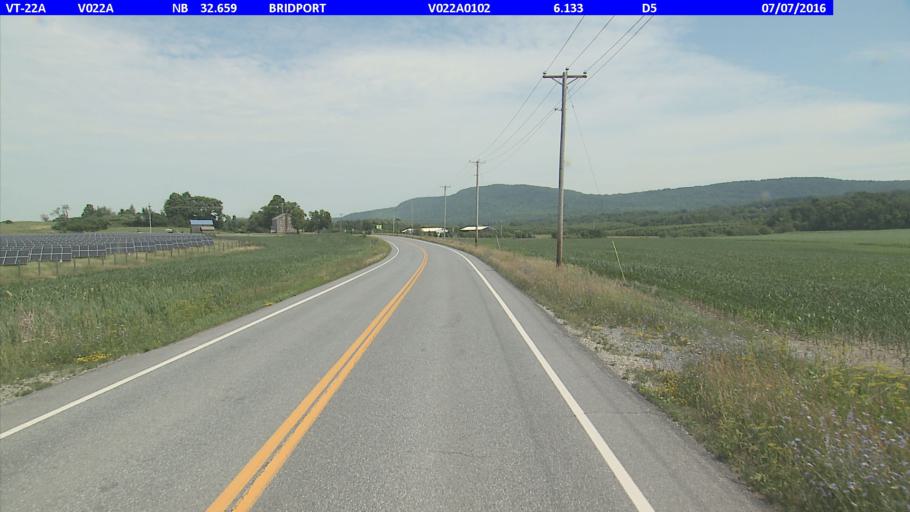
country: US
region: Vermont
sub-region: Addison County
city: Middlebury (village)
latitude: 44.0277
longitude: -73.3088
